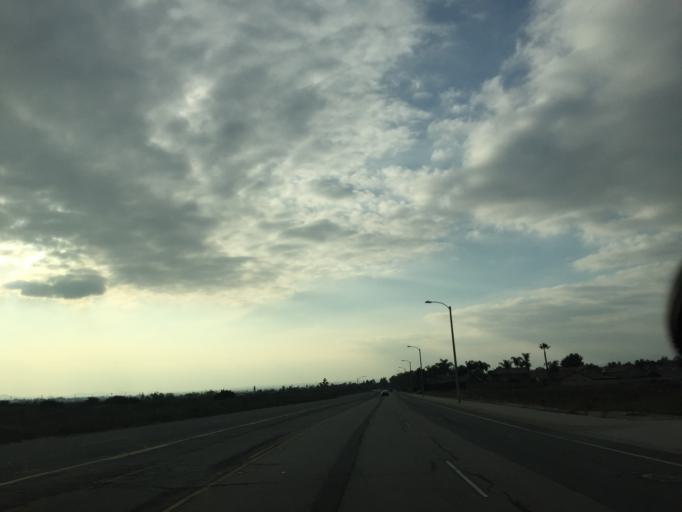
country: US
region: California
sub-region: San Bernardino County
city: Mentone
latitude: 34.1098
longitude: -117.1565
